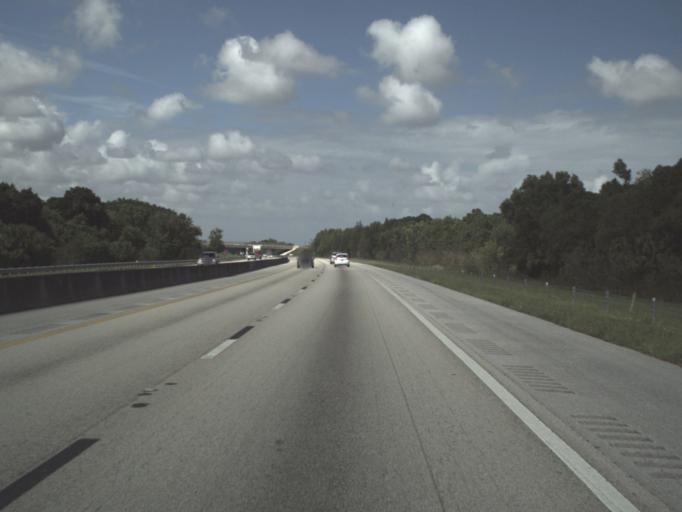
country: US
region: Florida
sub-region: Palm Beach County
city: Palm Beach Gardens
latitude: 26.8767
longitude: -80.1291
